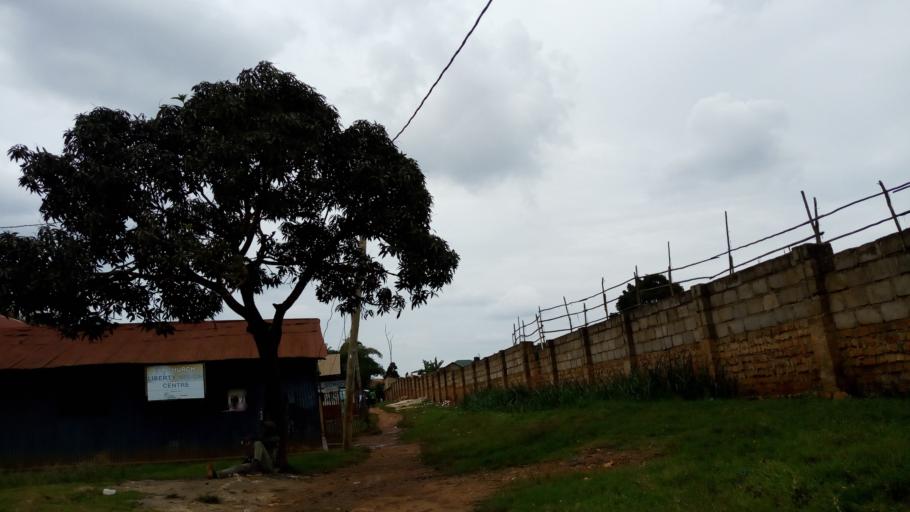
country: UG
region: Central Region
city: Kampala Central Division
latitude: 0.3584
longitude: 32.5609
